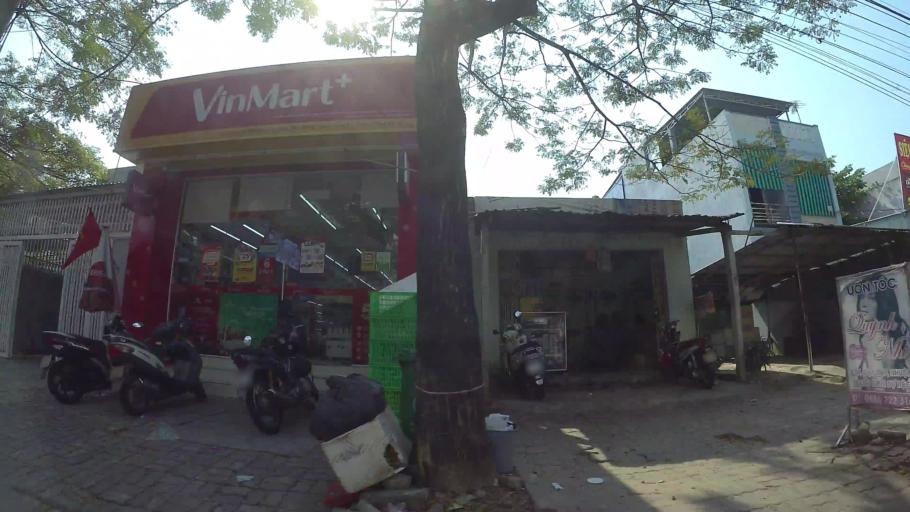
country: VN
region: Da Nang
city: Cam Le
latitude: 16.0065
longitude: 108.1949
